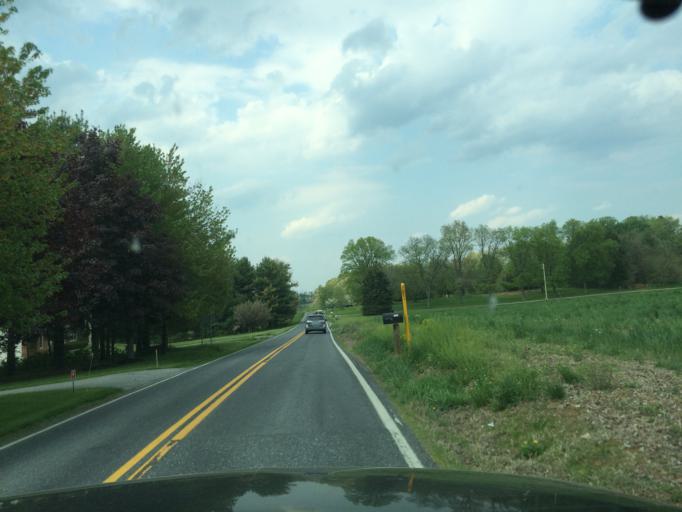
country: US
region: Maryland
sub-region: Carroll County
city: Sykesville
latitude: 39.2923
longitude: -76.9918
